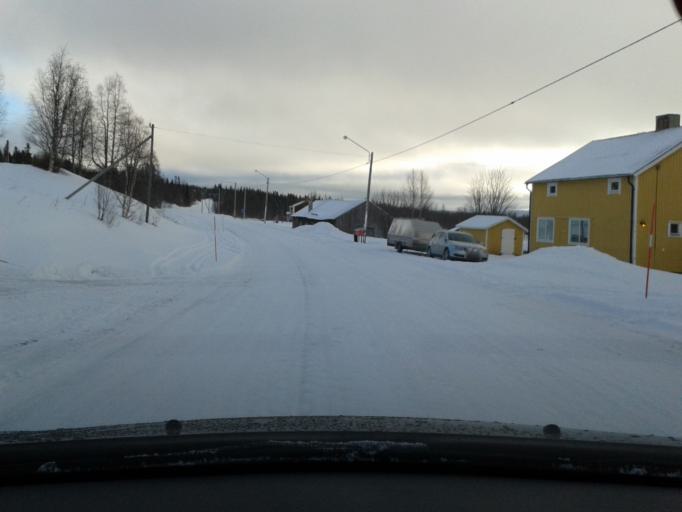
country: SE
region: Vaesterbotten
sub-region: Vilhelmina Kommun
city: Sjoberg
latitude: 65.2508
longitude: 15.5767
